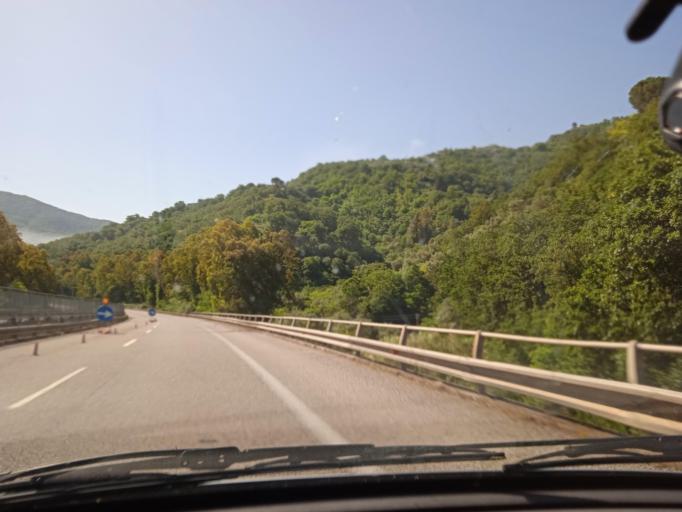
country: IT
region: Sicily
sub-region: Messina
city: Piraino
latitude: 38.1428
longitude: 14.8637
